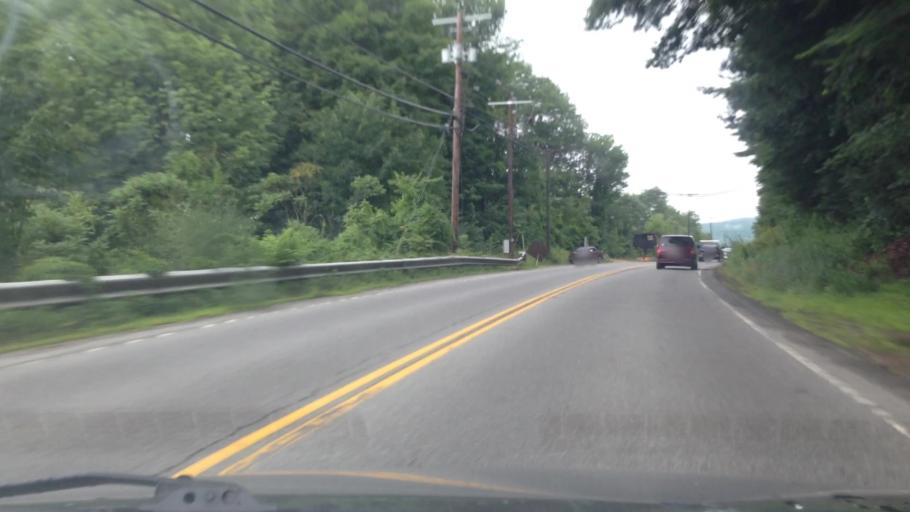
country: US
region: New Hampshire
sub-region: Cheshire County
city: Keene
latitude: 42.9149
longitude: -72.2522
